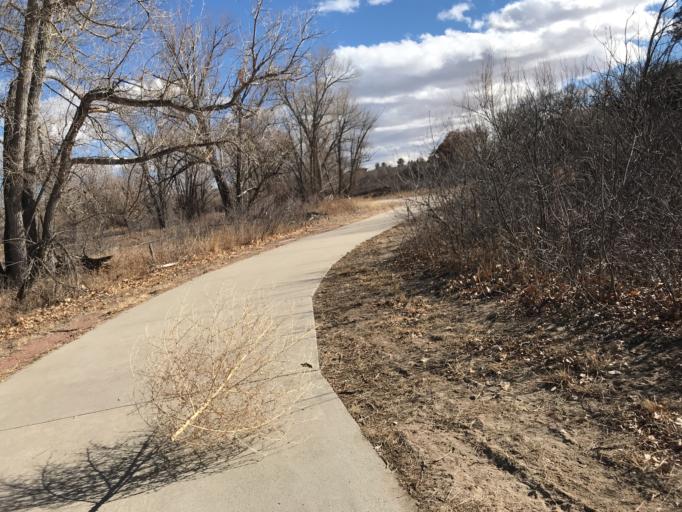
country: US
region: Colorado
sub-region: Douglas County
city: Castle Rock
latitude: 39.4097
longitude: -104.8827
